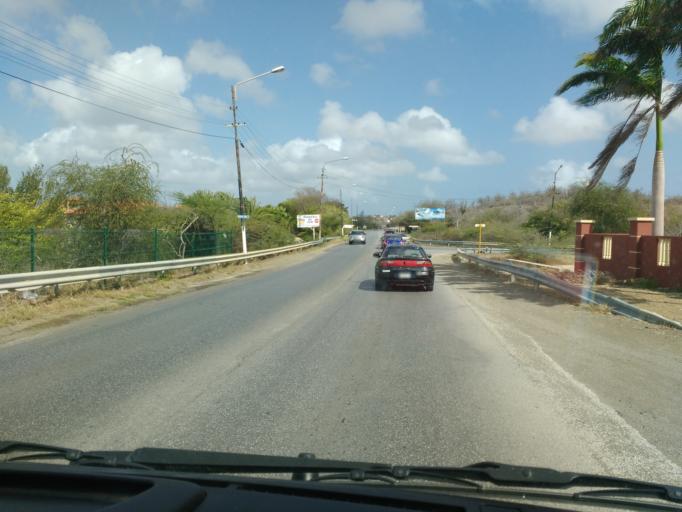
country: CW
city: Willemstad
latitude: 12.1007
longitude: -68.8759
